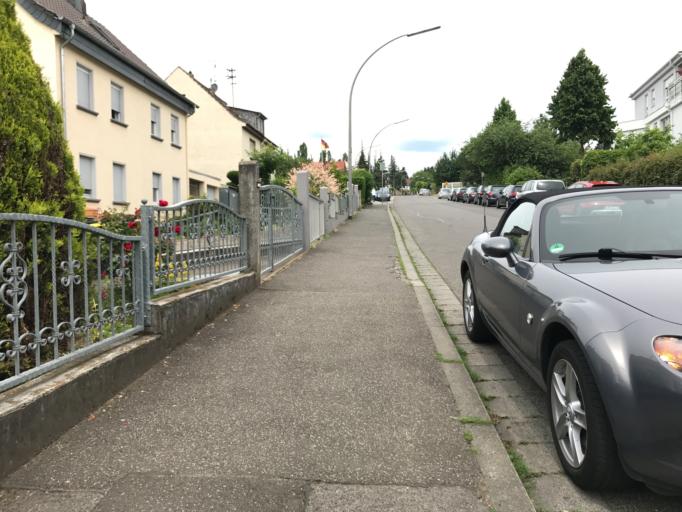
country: DE
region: Rheinland-Pfalz
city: Budenheim
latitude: 50.0494
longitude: 8.1923
